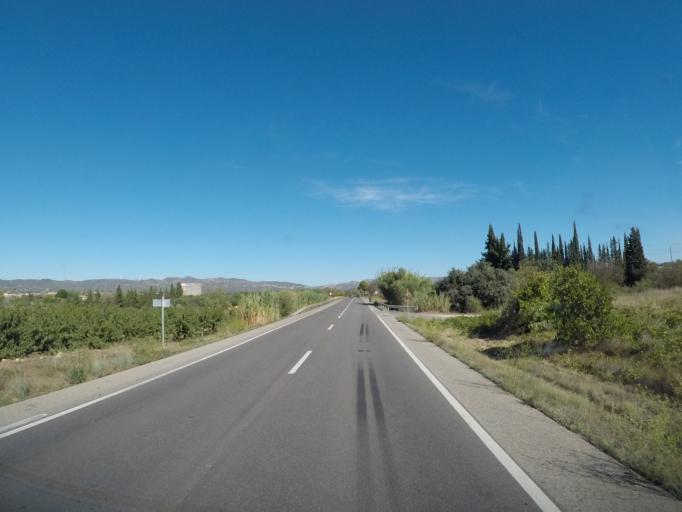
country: ES
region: Catalonia
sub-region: Provincia de Tarragona
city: Ginestar
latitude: 41.0806
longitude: 0.6613
